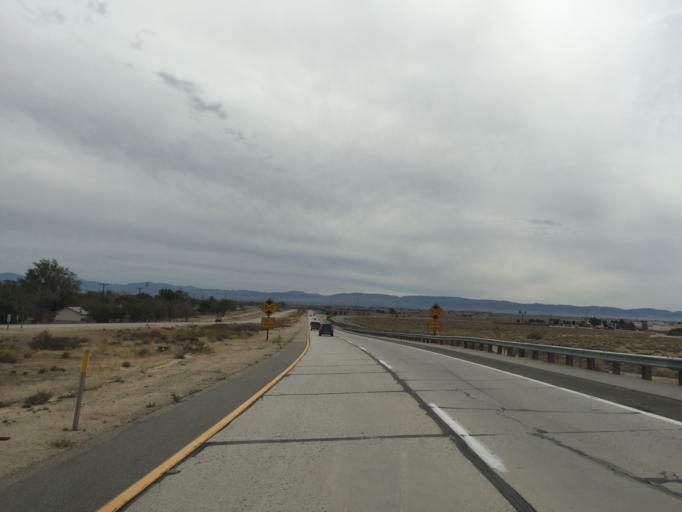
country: US
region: California
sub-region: Kern County
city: Rosamond
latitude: 34.8721
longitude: -118.1716
